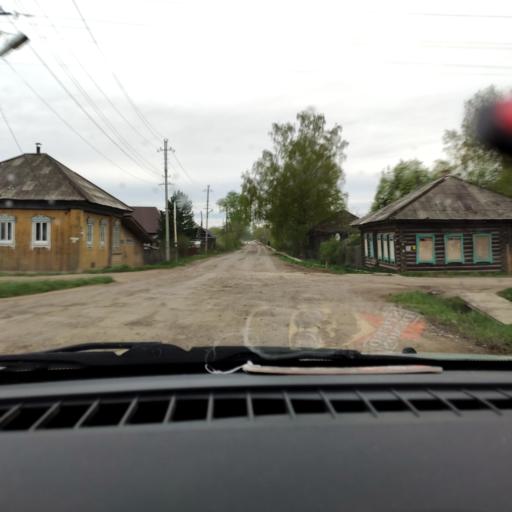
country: RU
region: Perm
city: Kudymkar
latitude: 59.0075
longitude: 54.6528
